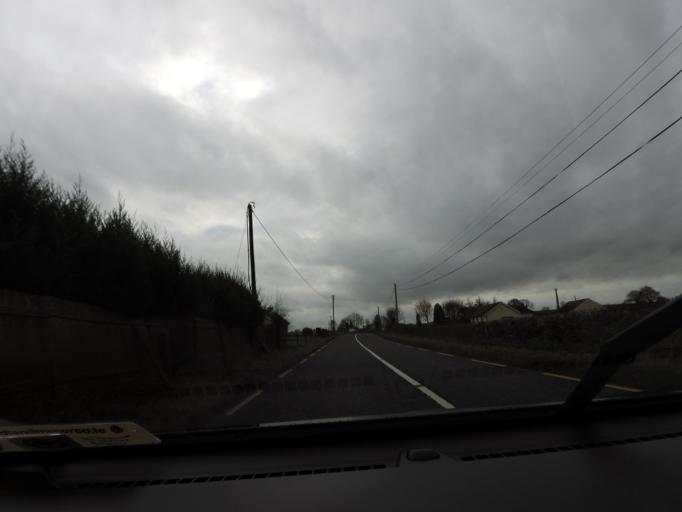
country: IE
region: Leinster
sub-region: Kilkenny
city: Ballyragget
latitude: 52.7288
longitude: -7.3098
